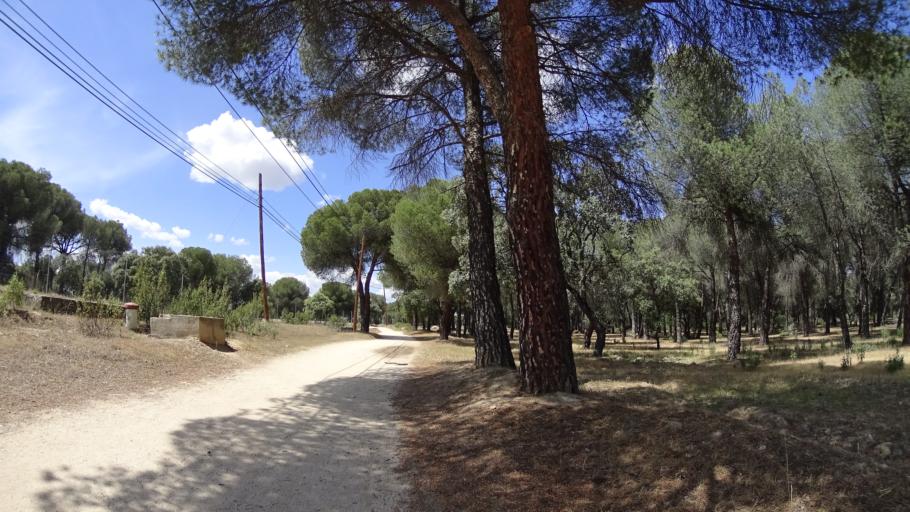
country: ES
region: Madrid
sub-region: Provincia de Madrid
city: Boadilla del Monte
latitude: 40.4358
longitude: -3.8755
